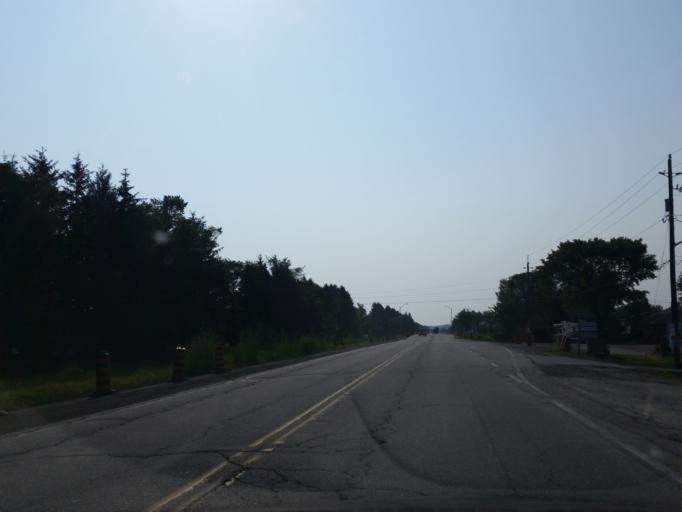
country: CA
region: Ontario
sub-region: Nipissing District
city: North Bay
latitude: 46.4131
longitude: -80.1265
